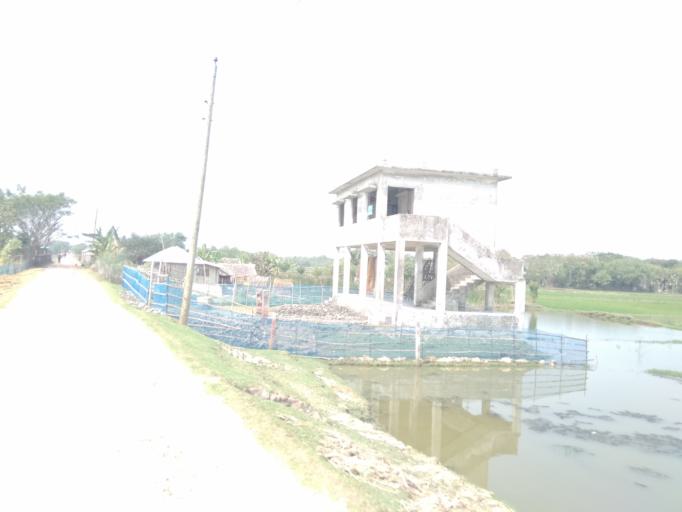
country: IN
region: West Bengal
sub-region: North 24 Parganas
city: Taki
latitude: 22.3036
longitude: 89.2671
